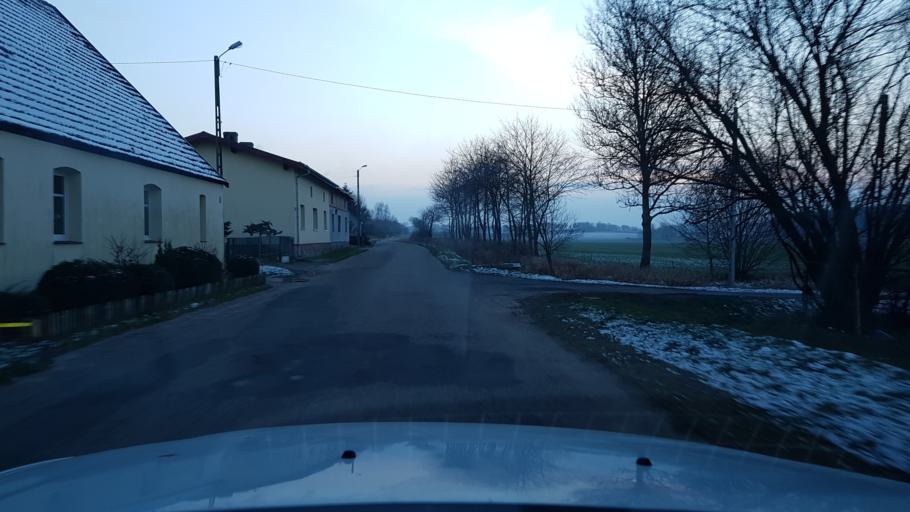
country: PL
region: West Pomeranian Voivodeship
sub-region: Powiat bialogardzki
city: Karlino
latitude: 53.9832
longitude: 15.7974
